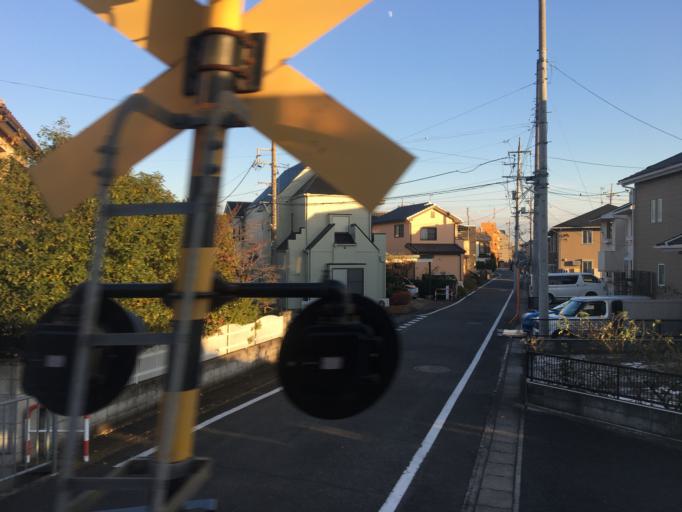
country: JP
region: Gunma
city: Takasaki
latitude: 36.3432
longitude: 139.0156
